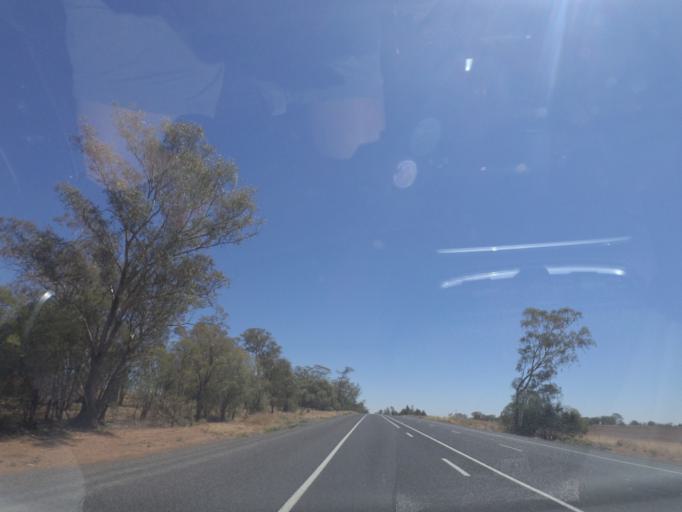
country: AU
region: New South Wales
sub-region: Gilgandra
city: Gilgandra
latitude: -31.4937
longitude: 148.8674
